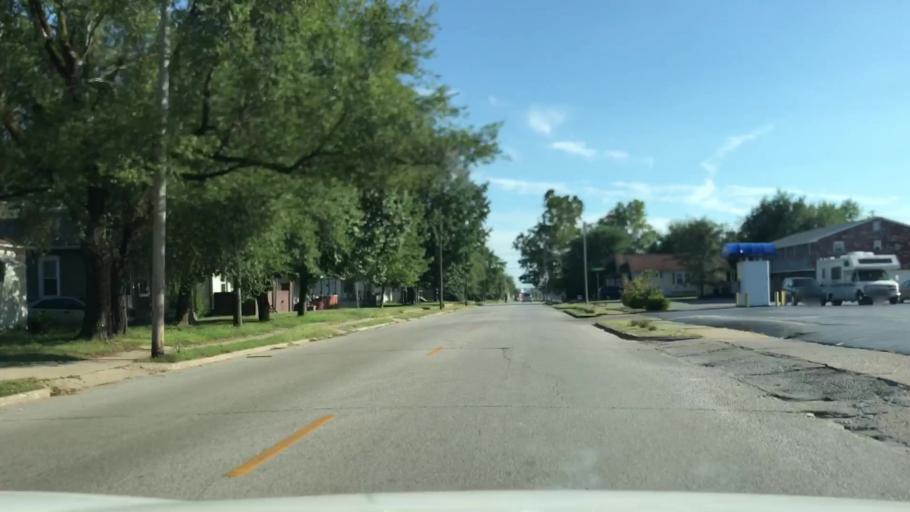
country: US
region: Illinois
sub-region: Madison County
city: Wood River
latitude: 38.8676
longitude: -90.0986
